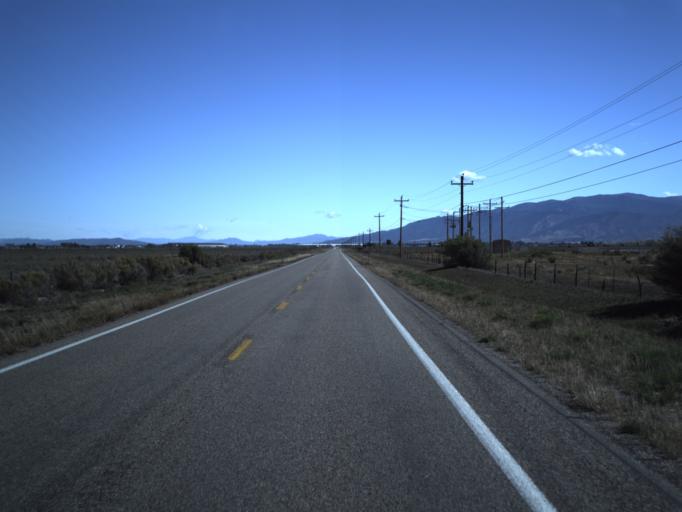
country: US
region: Utah
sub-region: Iron County
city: Cedar City
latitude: 37.6683
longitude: -113.1964
